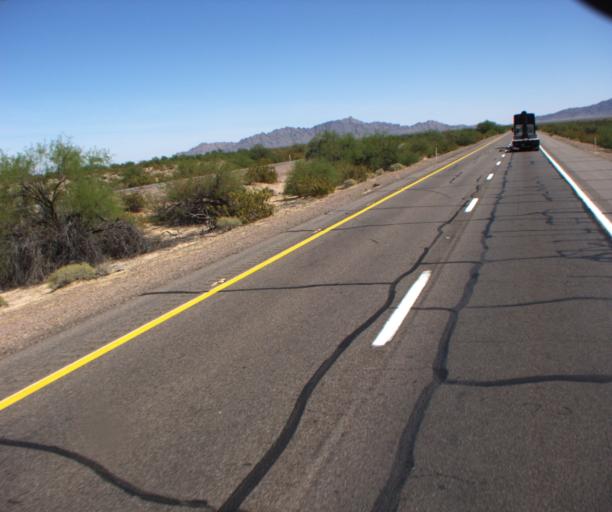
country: US
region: Arizona
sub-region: Yuma County
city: Wellton
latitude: 32.7048
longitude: -113.8779
